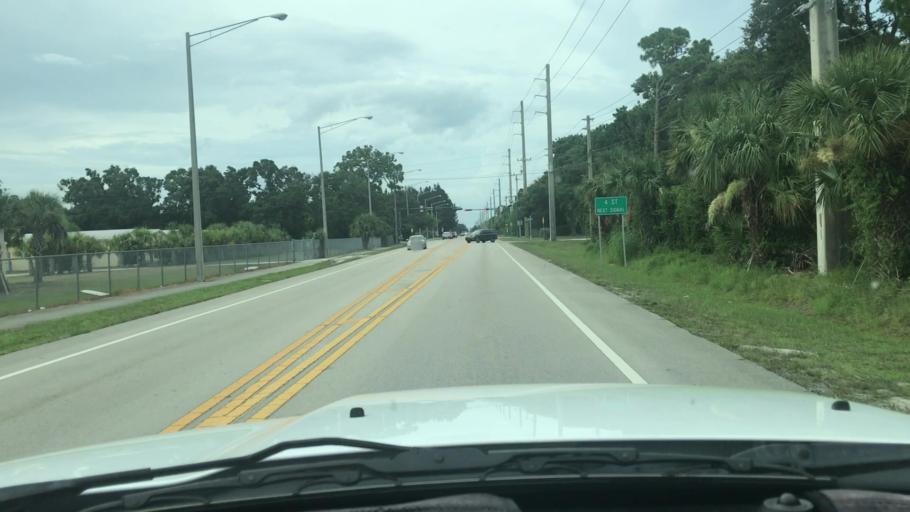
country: US
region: Florida
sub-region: Indian River County
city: Vero Beach South
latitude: 27.6075
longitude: -80.4140
